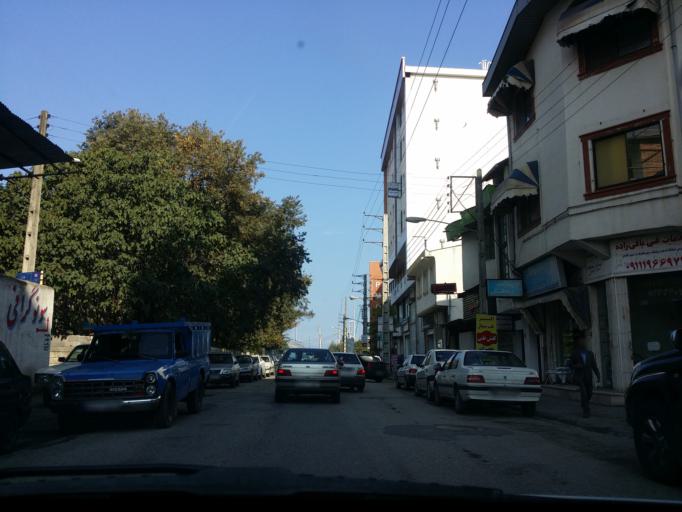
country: IR
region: Mazandaran
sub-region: Nowshahr
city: Nowshahr
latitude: 36.6505
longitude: 51.5086
